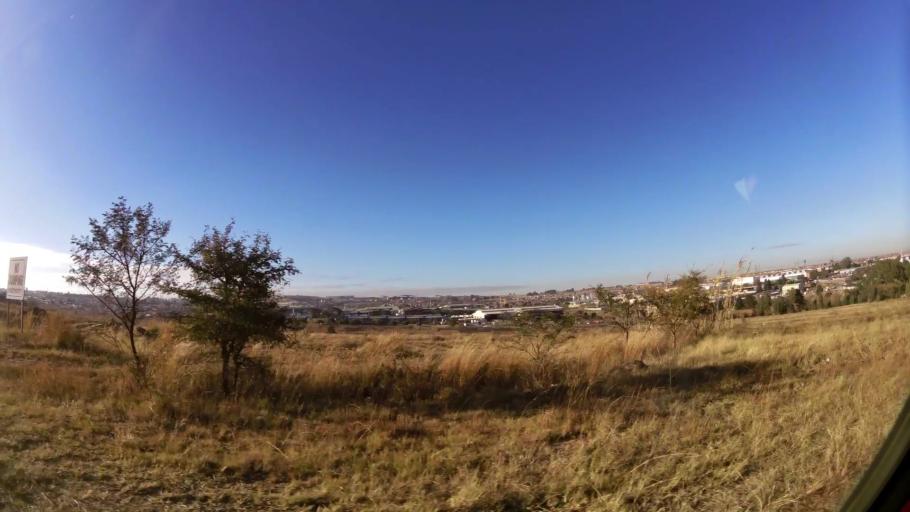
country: ZA
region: Gauteng
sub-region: City of Johannesburg Metropolitan Municipality
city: Midrand
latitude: -26.0303
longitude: 28.1506
